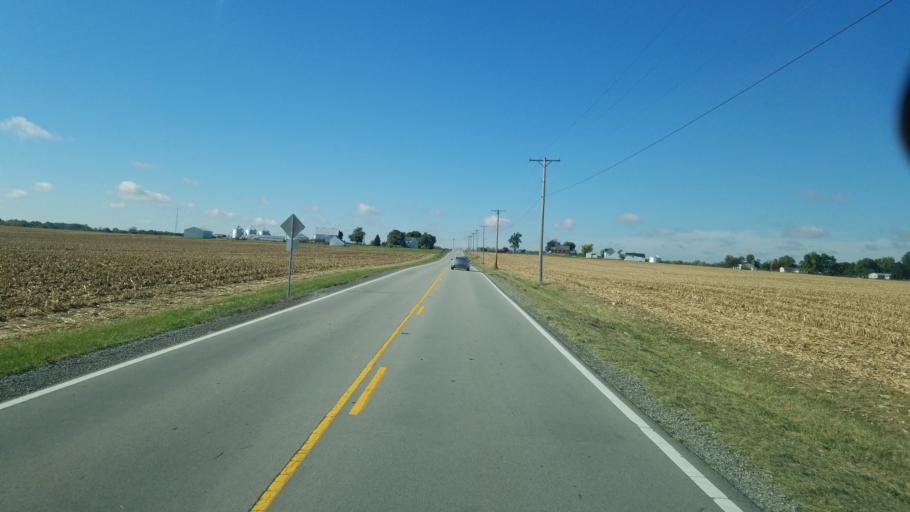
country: US
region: Ohio
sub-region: Fayette County
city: Washington Court House
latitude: 39.4502
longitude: -83.4963
